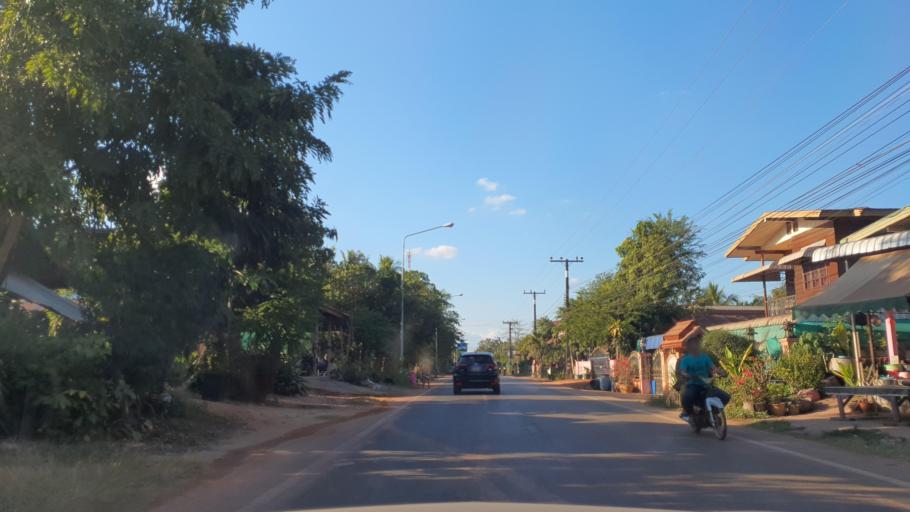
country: TH
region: Changwat Bueng Kan
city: Si Wilai
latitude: 18.1497
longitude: 103.9055
